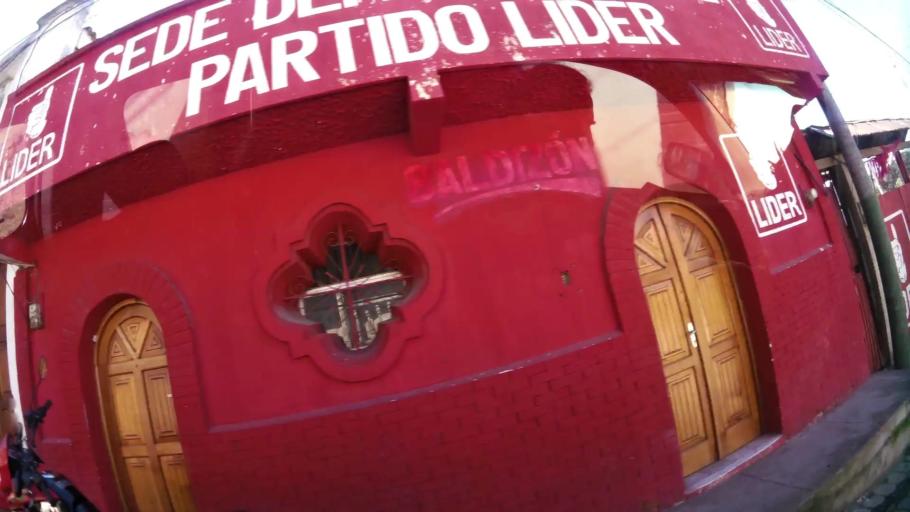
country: GT
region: Solola
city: Solola
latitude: 14.7759
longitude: -91.1821
